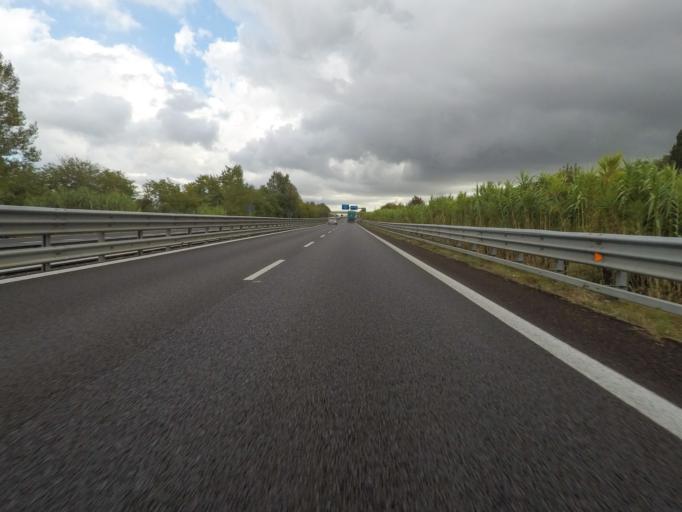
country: IT
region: Tuscany
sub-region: Provincia di Siena
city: Arbia
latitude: 43.3050
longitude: 11.4221
